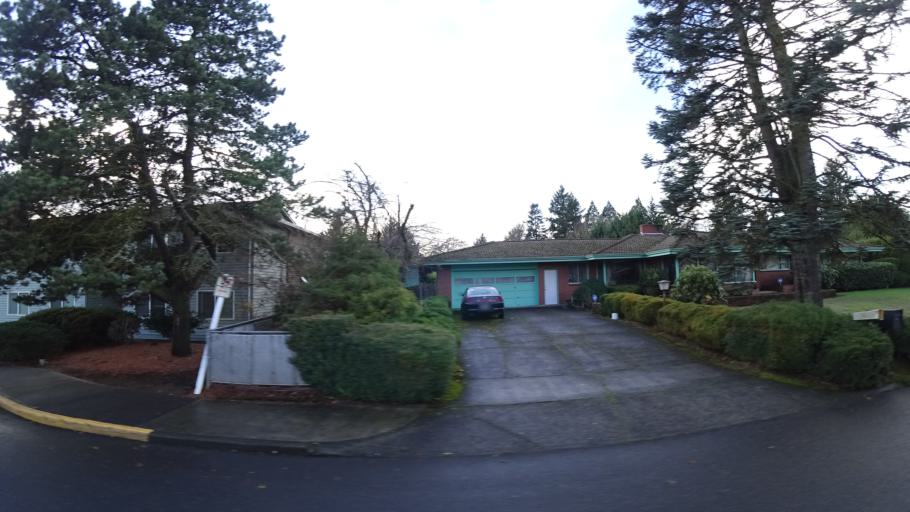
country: US
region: Oregon
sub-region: Multnomah County
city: Lents
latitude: 45.5195
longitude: -122.5494
